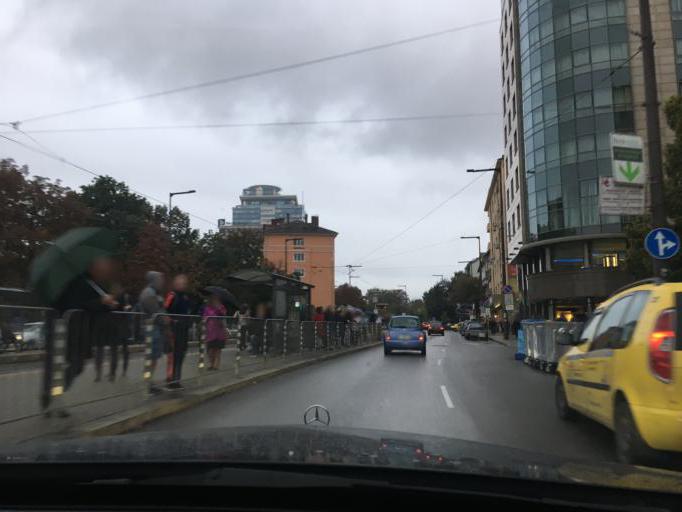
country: BG
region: Sofia-Capital
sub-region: Stolichna Obshtina
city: Sofia
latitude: 42.6860
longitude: 23.3177
